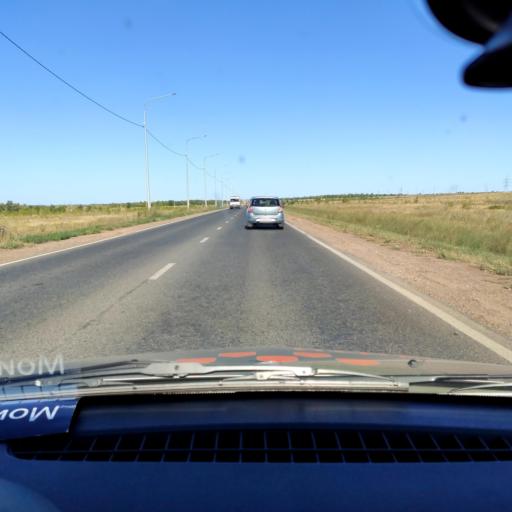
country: RU
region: Orenburg
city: Prigorodnyy
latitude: 51.8135
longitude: 55.1882
